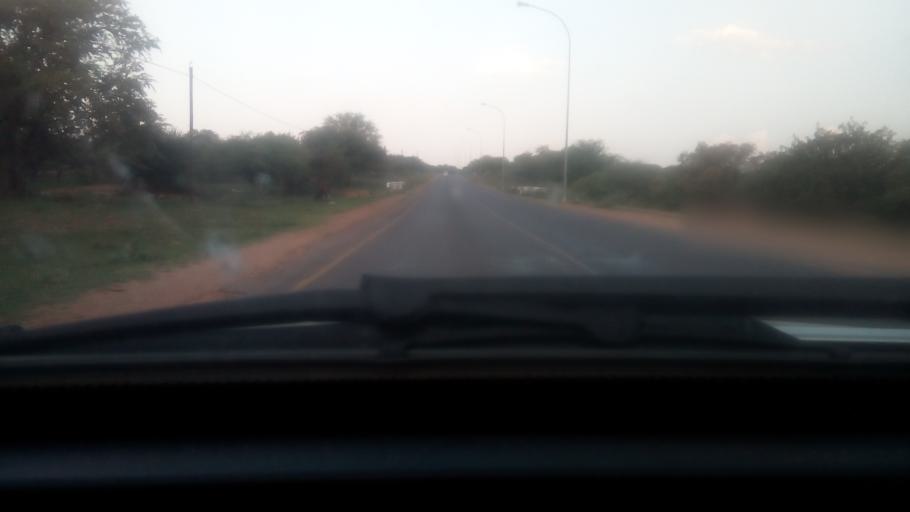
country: BW
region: Kgatleng
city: Bokaa
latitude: -24.4347
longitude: 26.0376
